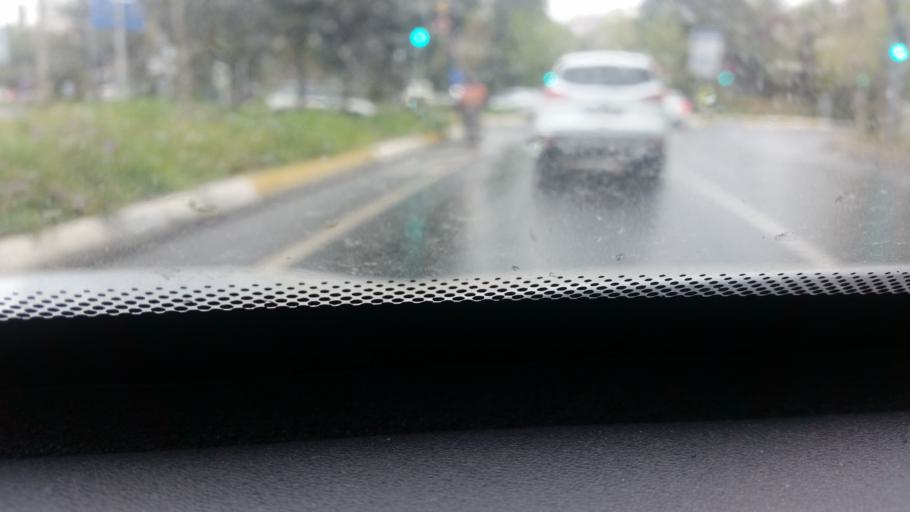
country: TR
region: Istanbul
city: Bahcelievler
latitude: 40.9829
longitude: 28.8534
